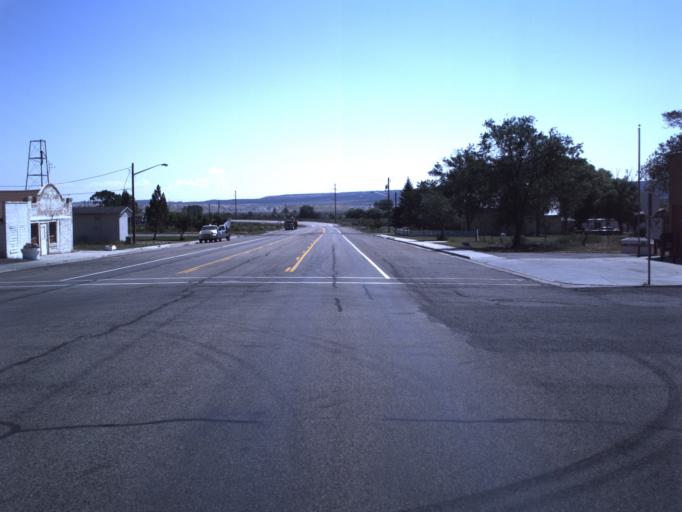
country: US
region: Utah
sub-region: Emery County
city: Ferron
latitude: 38.9231
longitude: -111.2488
